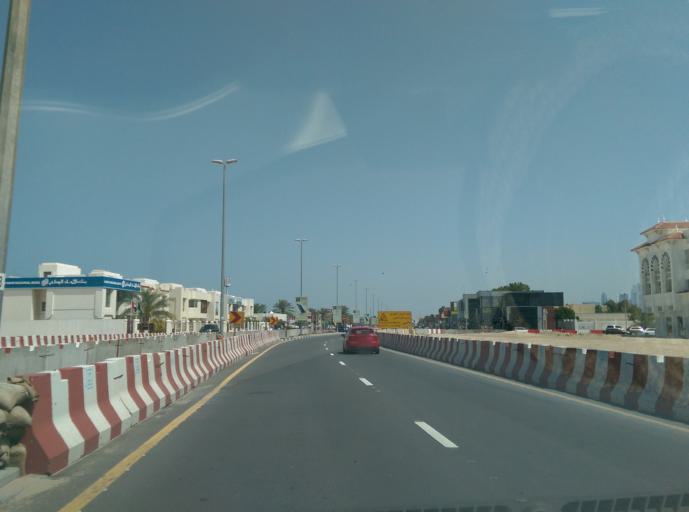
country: AE
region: Dubai
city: Dubai
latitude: 25.1950
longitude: 55.2456
